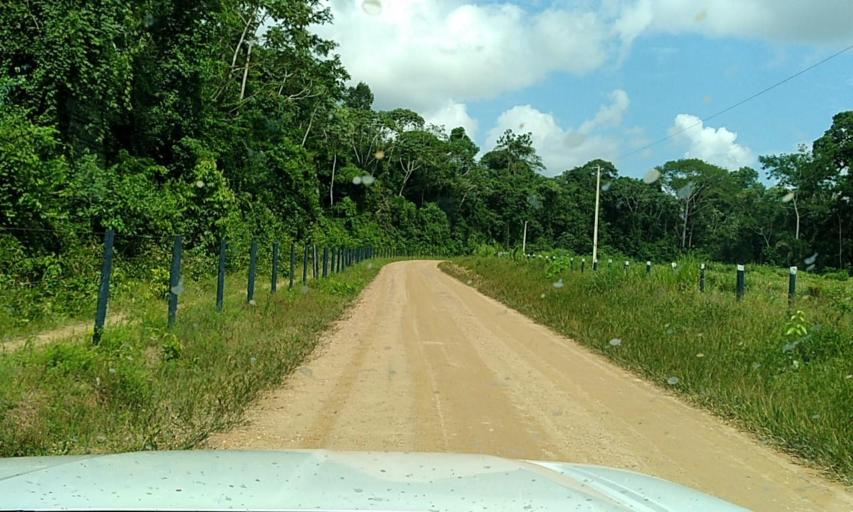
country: BR
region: Para
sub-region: Senador Jose Porfirio
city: Senador Jose Porfirio
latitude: -2.5207
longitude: -51.8362
